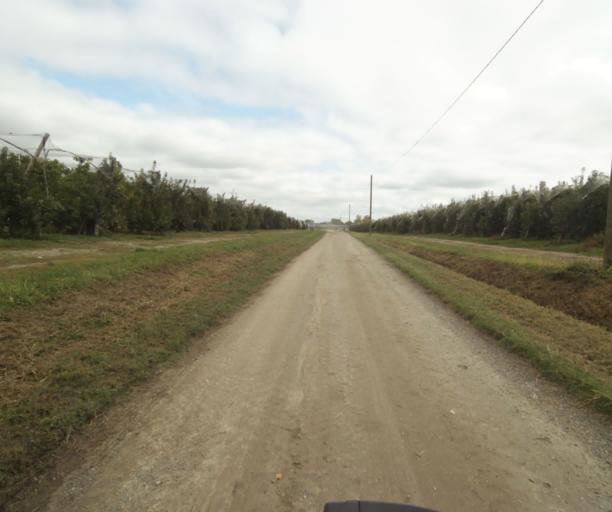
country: FR
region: Midi-Pyrenees
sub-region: Departement du Tarn-et-Garonne
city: Montech
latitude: 43.9584
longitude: 1.2017
